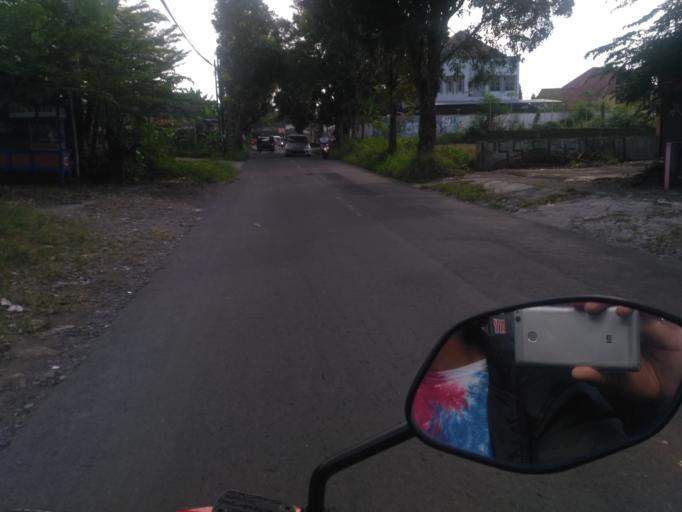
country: ID
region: Daerah Istimewa Yogyakarta
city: Yogyakarta
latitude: -7.7650
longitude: 110.3445
